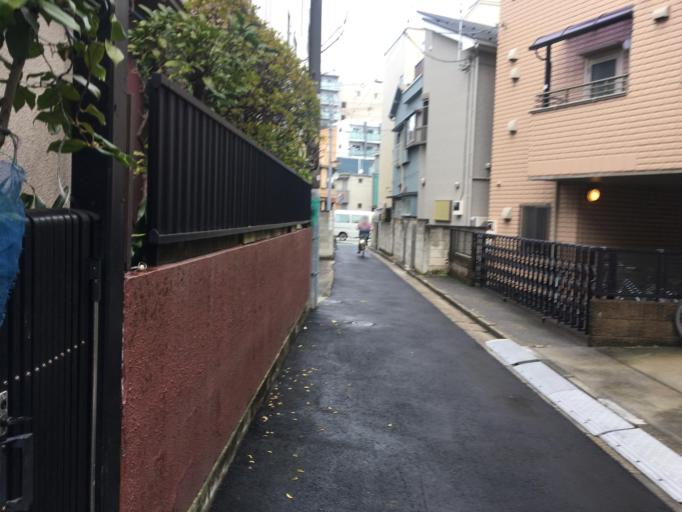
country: JP
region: Tokyo
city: Urayasu
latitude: 35.7003
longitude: 139.8323
